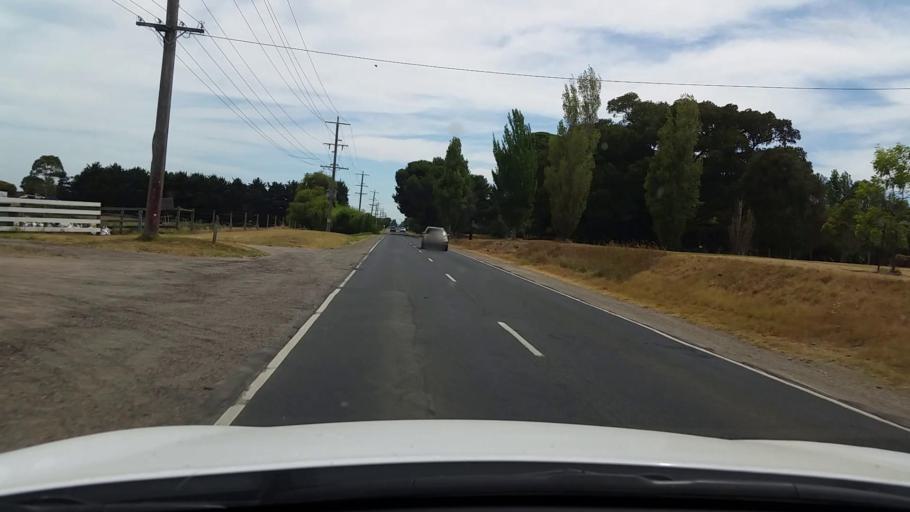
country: AU
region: Victoria
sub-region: Mornington Peninsula
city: Rosebud West
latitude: -38.3934
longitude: 144.8883
